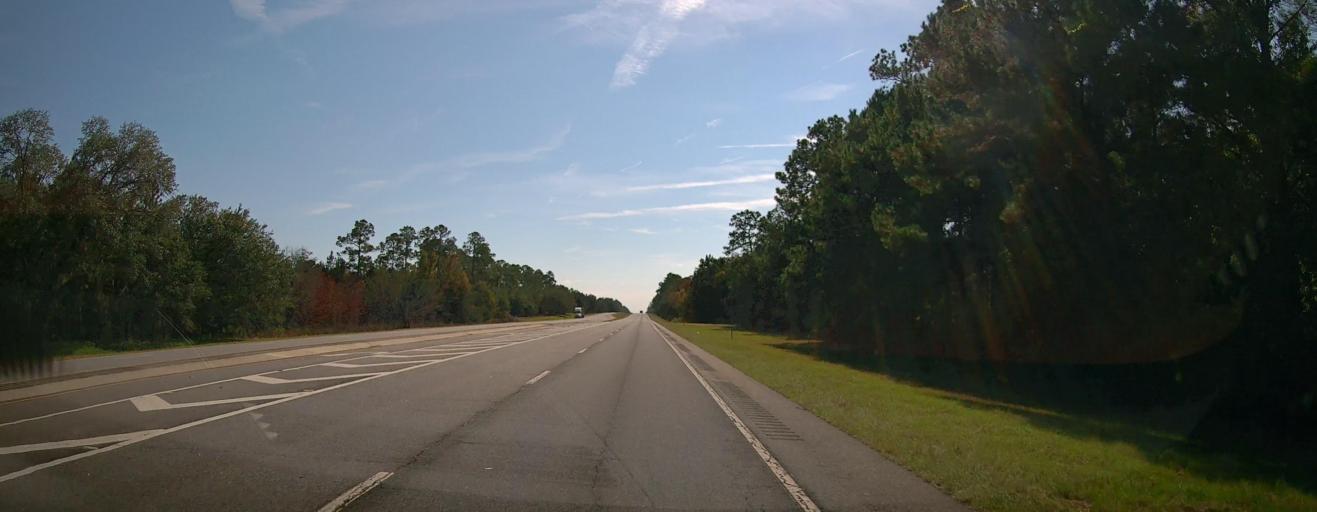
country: US
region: Georgia
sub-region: Lee County
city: Leesburg
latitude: 31.7004
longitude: -83.9915
